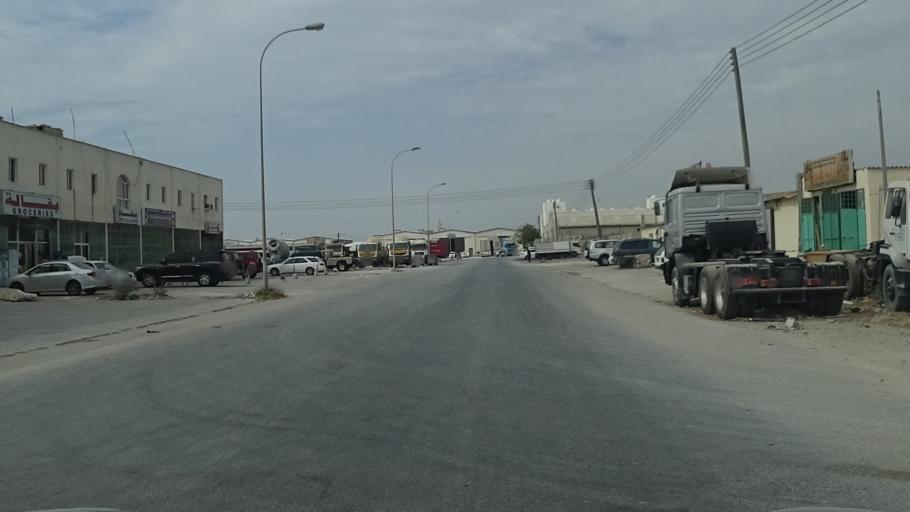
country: OM
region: Zufar
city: Salalah
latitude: 17.0267
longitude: 54.0489
